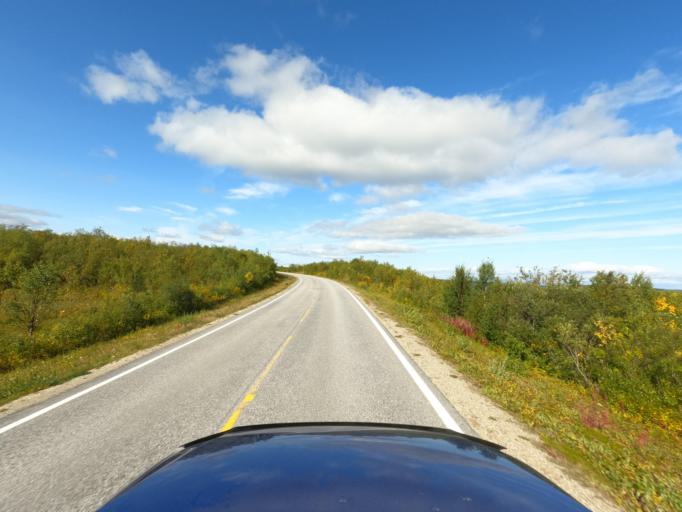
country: NO
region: Finnmark Fylke
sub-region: Karasjok
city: Karasjohka
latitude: 69.6075
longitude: 25.3203
